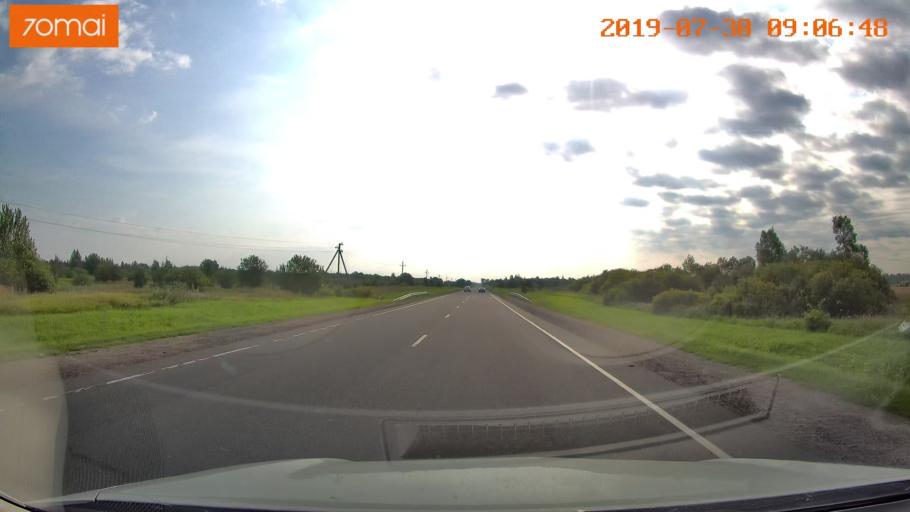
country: RU
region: Kaliningrad
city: Gusev
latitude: 54.6102
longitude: 22.3464
